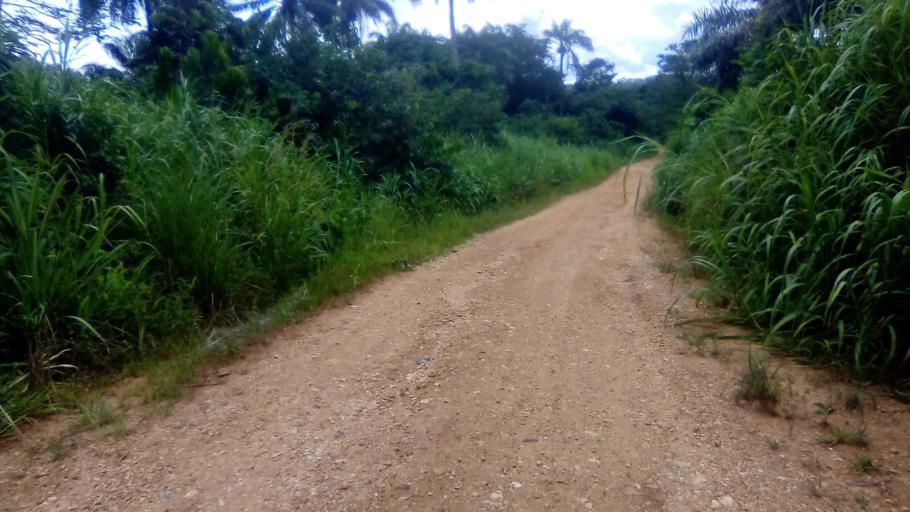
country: SL
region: Eastern Province
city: Simbakoro
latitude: 8.5473
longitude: -10.9304
